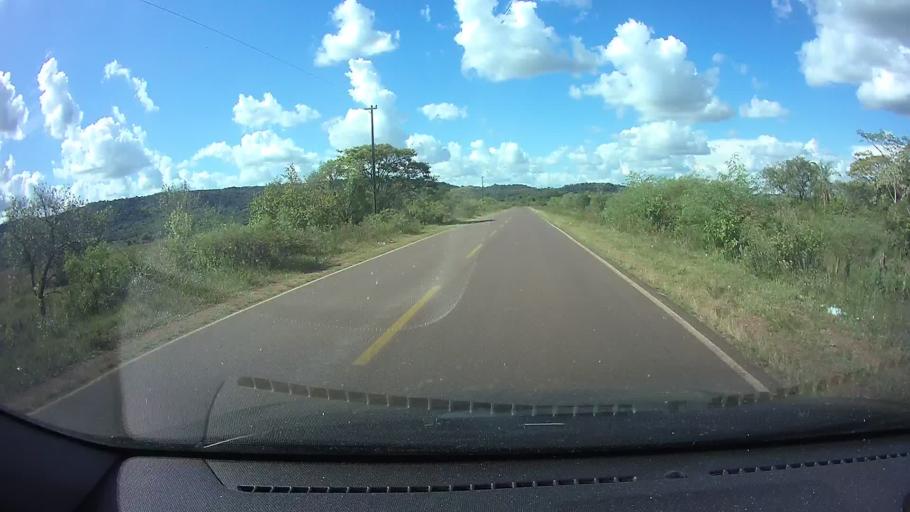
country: PY
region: Paraguari
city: Sapucai
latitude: -25.6827
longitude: -56.8631
